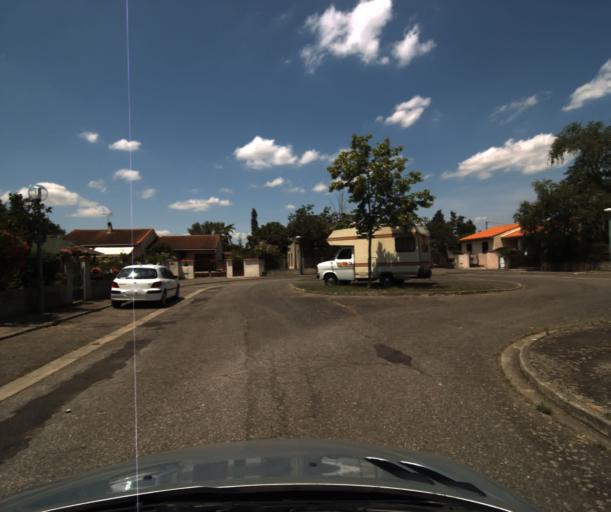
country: FR
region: Midi-Pyrenees
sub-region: Departement de la Haute-Garonne
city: Saint-Lys
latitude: 43.5097
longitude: 1.1754
